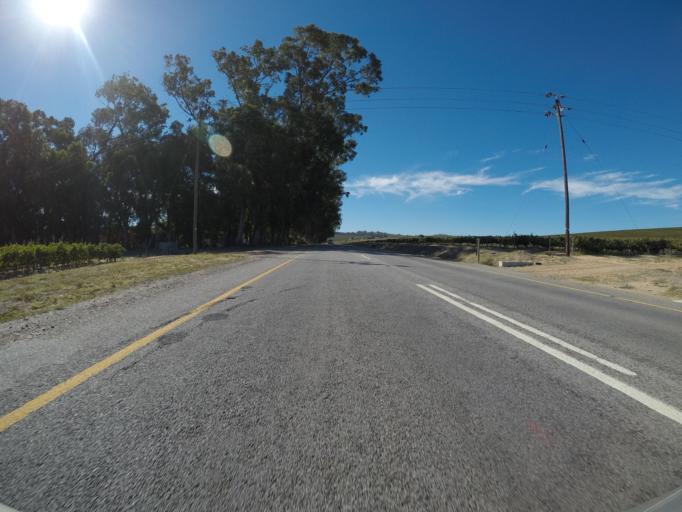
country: ZA
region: Western Cape
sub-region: Cape Winelands District Municipality
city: Stellenbosch
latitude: -33.9838
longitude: 18.7550
